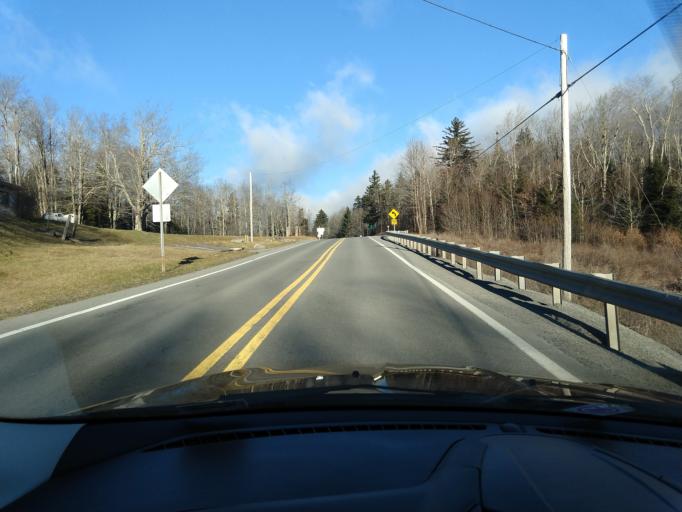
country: US
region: Virginia
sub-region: Highland County
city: Monterey
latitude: 38.5979
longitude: -79.8485
